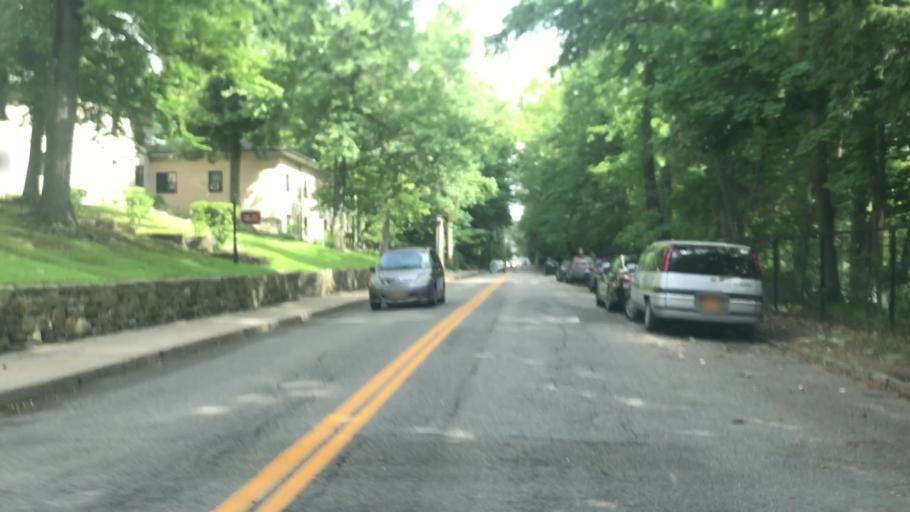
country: US
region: New York
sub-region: Westchester County
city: Tuckahoe
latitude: 40.9607
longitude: -73.8056
